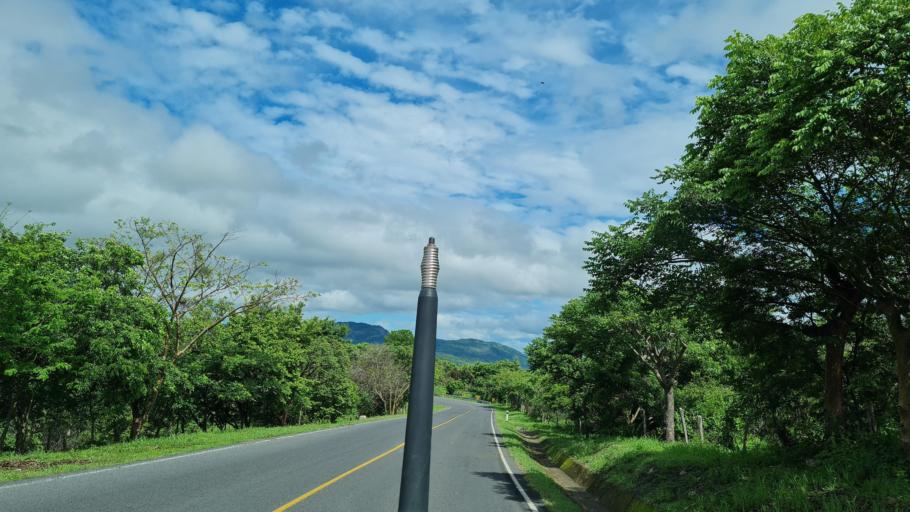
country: NI
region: Boaco
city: San Jose de los Remates
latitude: 12.6129
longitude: -85.8776
